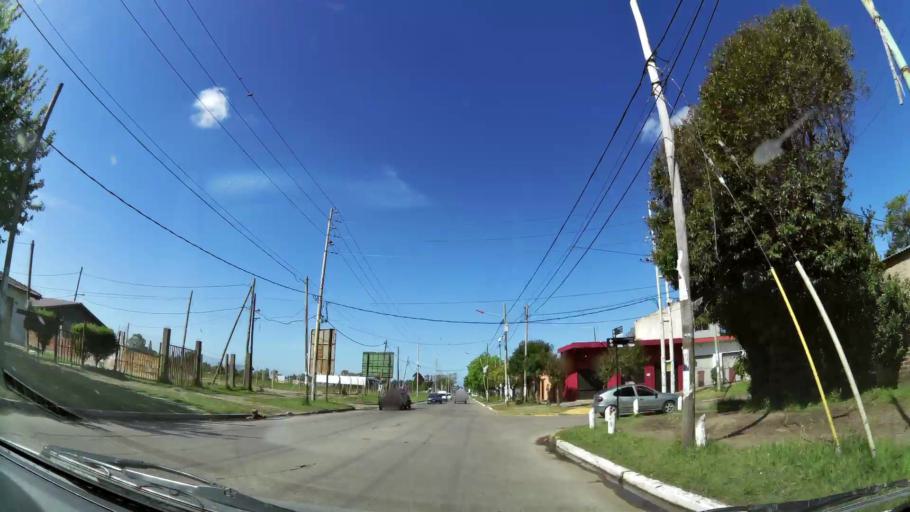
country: AR
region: Buenos Aires
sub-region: Partido de Quilmes
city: Quilmes
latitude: -34.7959
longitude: -58.2559
